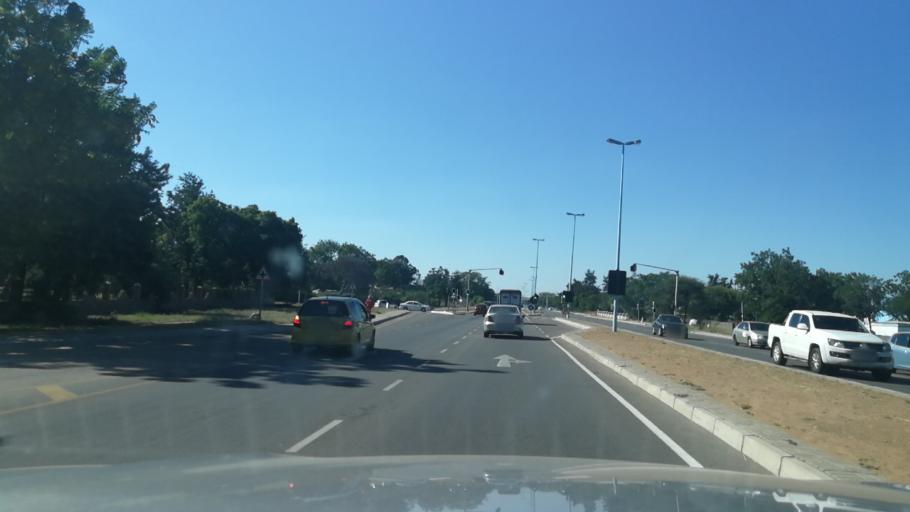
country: BW
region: South East
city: Gaborone
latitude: -24.6763
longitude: 25.9207
